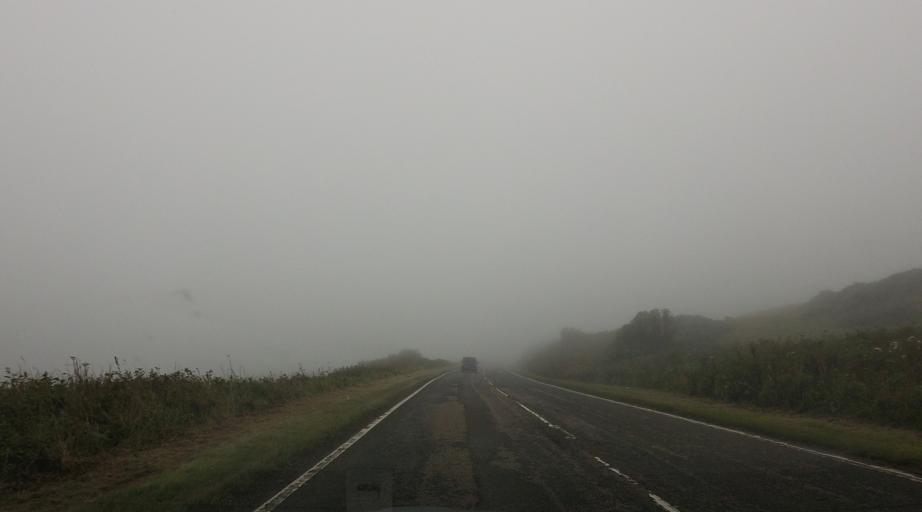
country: GB
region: Scotland
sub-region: Highland
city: Wick
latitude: 58.2657
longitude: -3.3949
